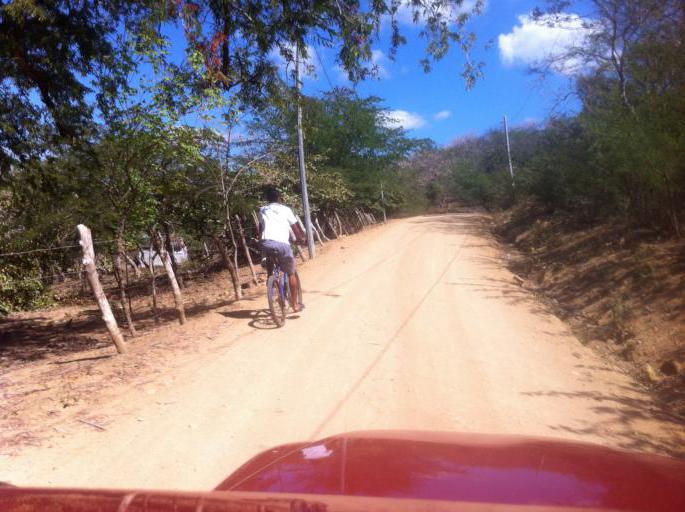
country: NI
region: Carazo
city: Santa Teresa
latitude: 11.6185
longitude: -86.3227
